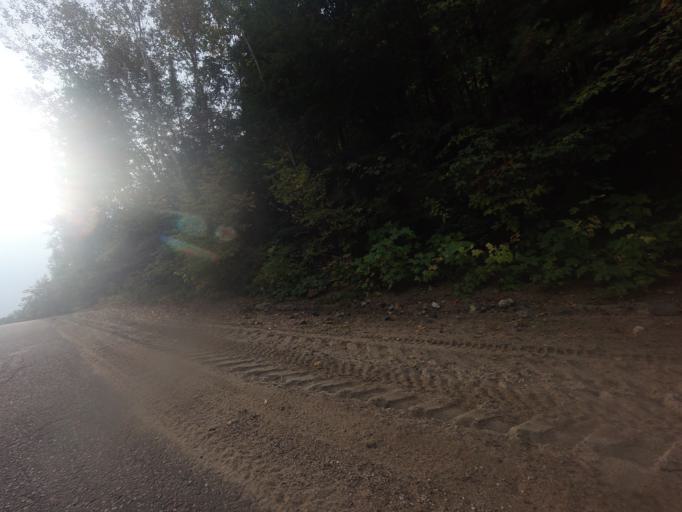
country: CA
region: Quebec
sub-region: Outaouais
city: Maniwaki
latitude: 46.0845
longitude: -76.0295
